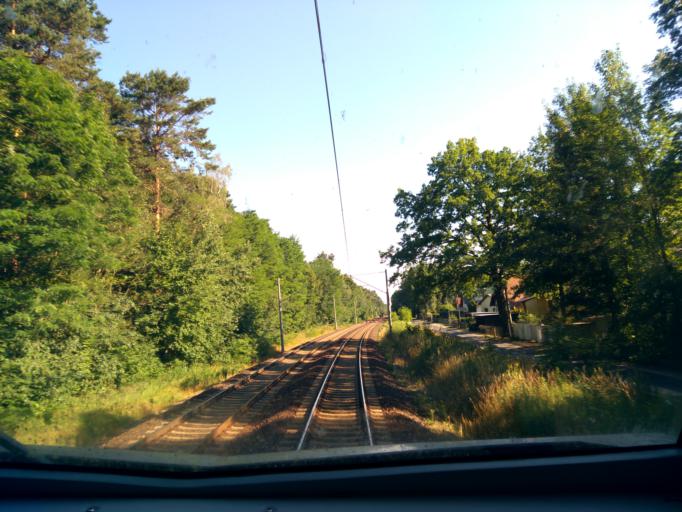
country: DE
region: Brandenburg
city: Bestensee
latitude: 52.2510
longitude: 13.6328
